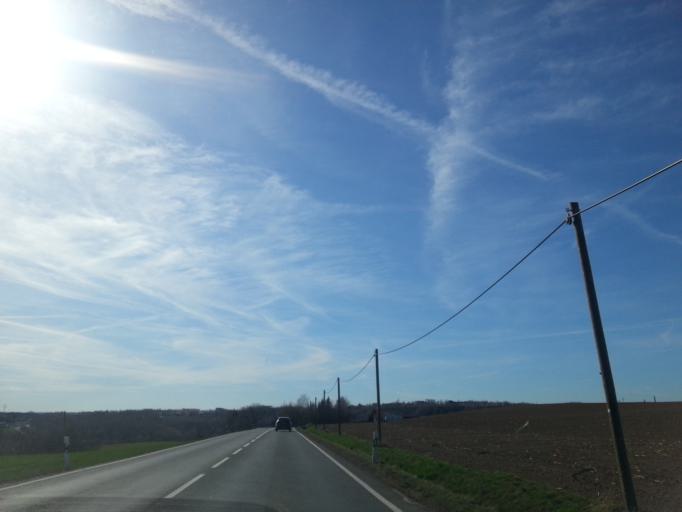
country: DE
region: Saxony
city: Halsbrucke
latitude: 50.9224
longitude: 13.3864
